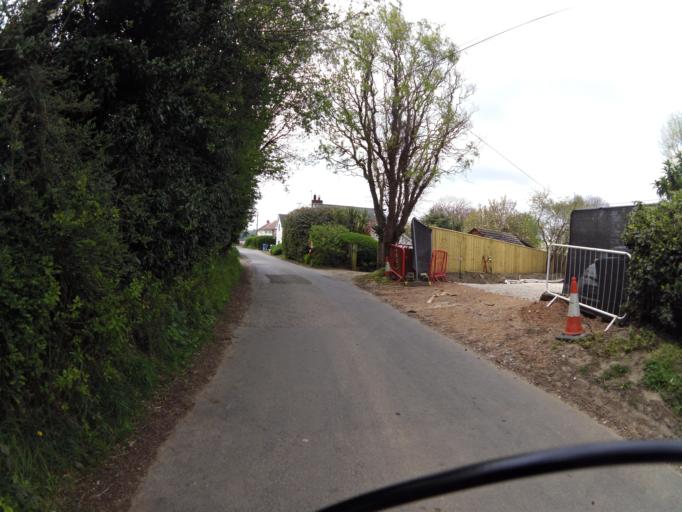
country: GB
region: England
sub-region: Suffolk
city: Hadleigh
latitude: 52.0507
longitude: 0.8935
